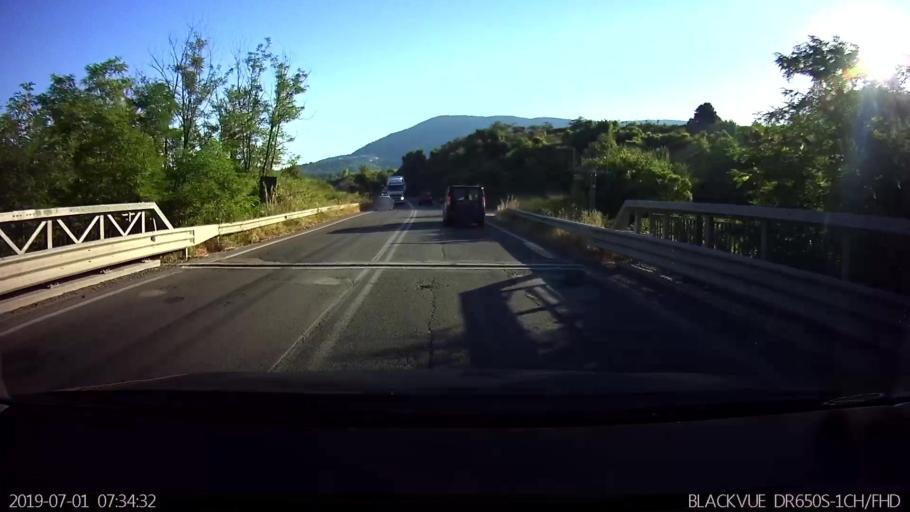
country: IT
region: Latium
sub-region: Provincia di Latina
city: Prossedi
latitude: 41.5164
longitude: 13.2723
